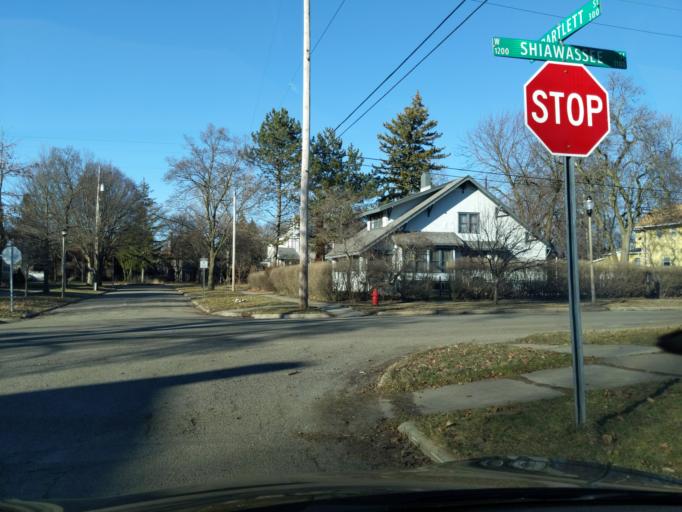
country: US
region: Michigan
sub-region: Ingham County
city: Lansing
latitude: 42.7372
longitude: -84.5687
